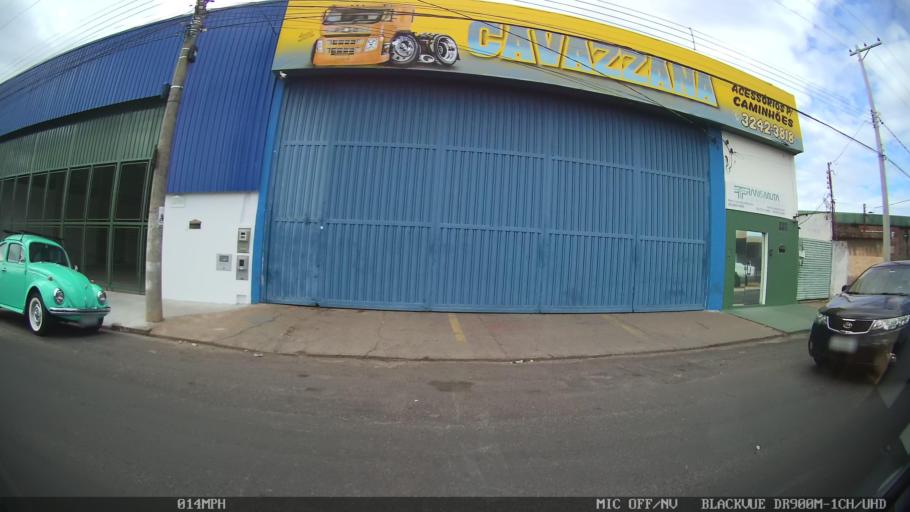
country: BR
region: Sao Paulo
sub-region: Sao Jose Do Rio Preto
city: Sao Jose do Rio Preto
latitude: -20.8119
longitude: -49.4924
